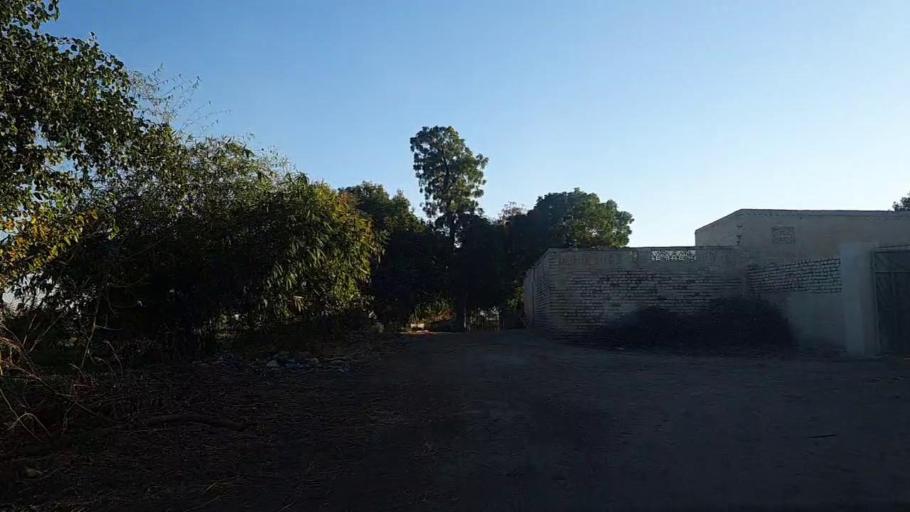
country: PK
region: Sindh
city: Sanghar
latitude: 26.1379
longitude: 68.9435
